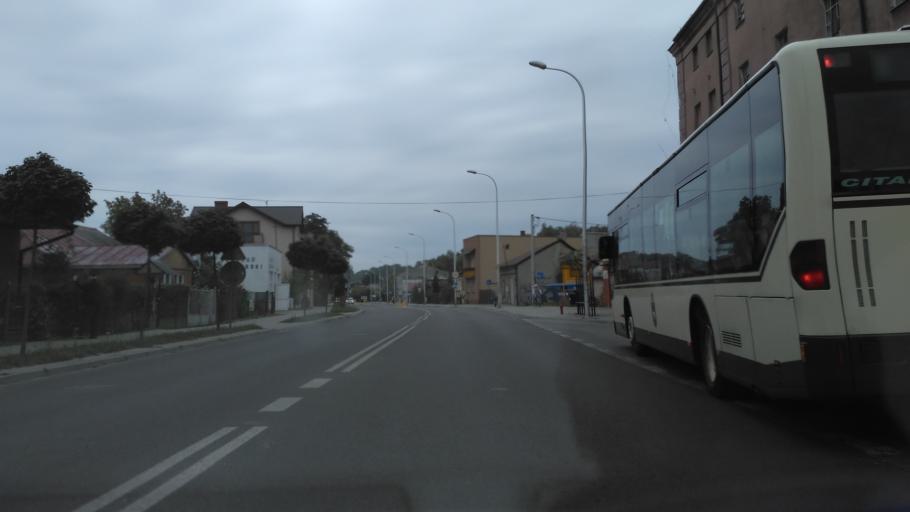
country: PL
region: Lublin Voivodeship
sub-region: Chelm
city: Chelm
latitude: 51.1380
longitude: 23.4613
